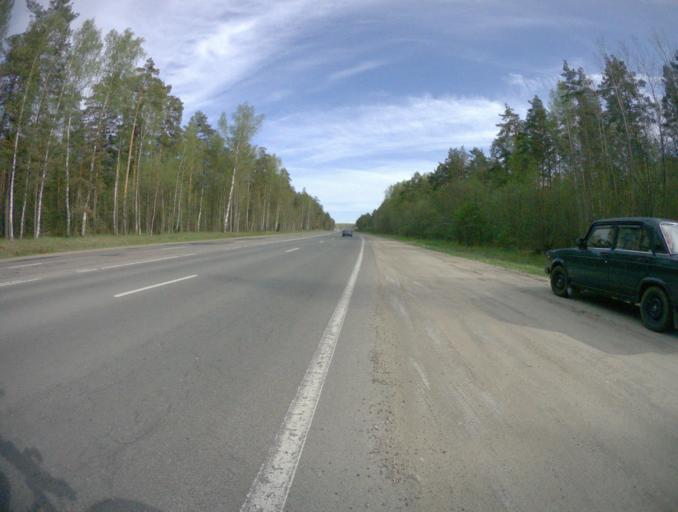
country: RU
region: Vladimir
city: Kommunar
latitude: 56.0890
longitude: 40.4553
